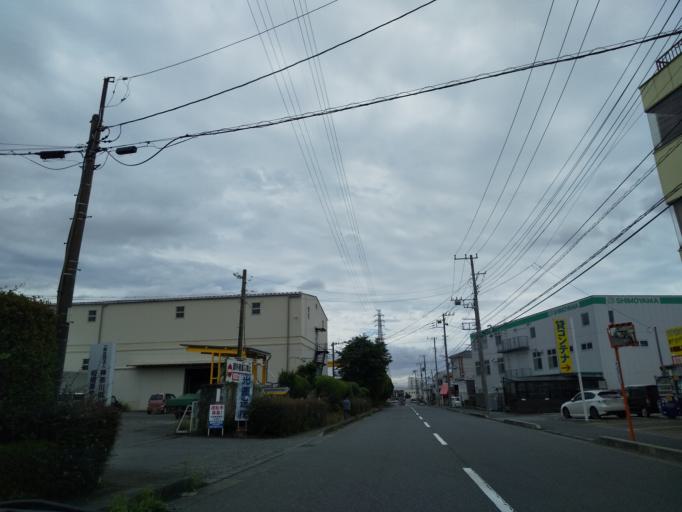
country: JP
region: Kanagawa
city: Zama
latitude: 35.5141
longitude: 139.3409
